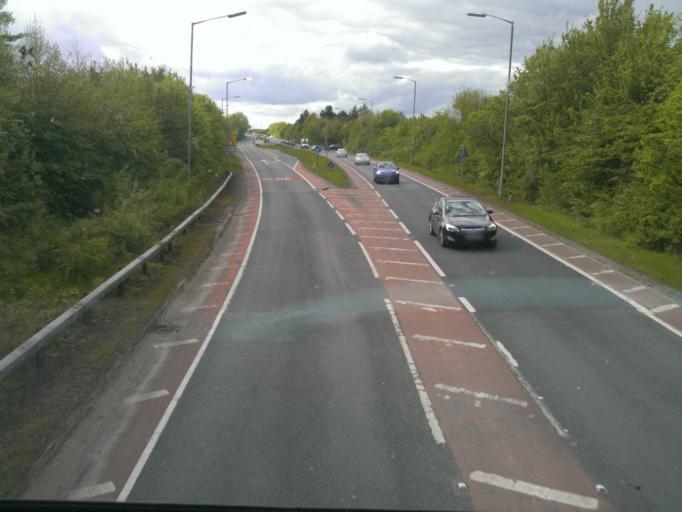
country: GB
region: England
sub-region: Essex
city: Coggeshall
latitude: 51.8796
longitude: 0.6955
